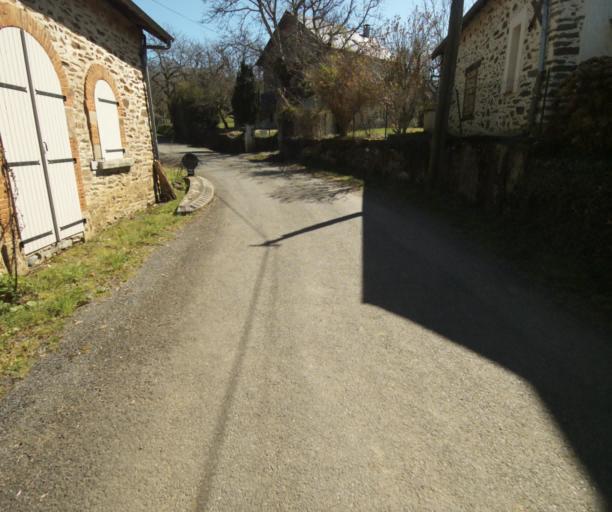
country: FR
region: Limousin
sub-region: Departement de la Correze
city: Uzerche
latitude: 45.4072
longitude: 1.6172
